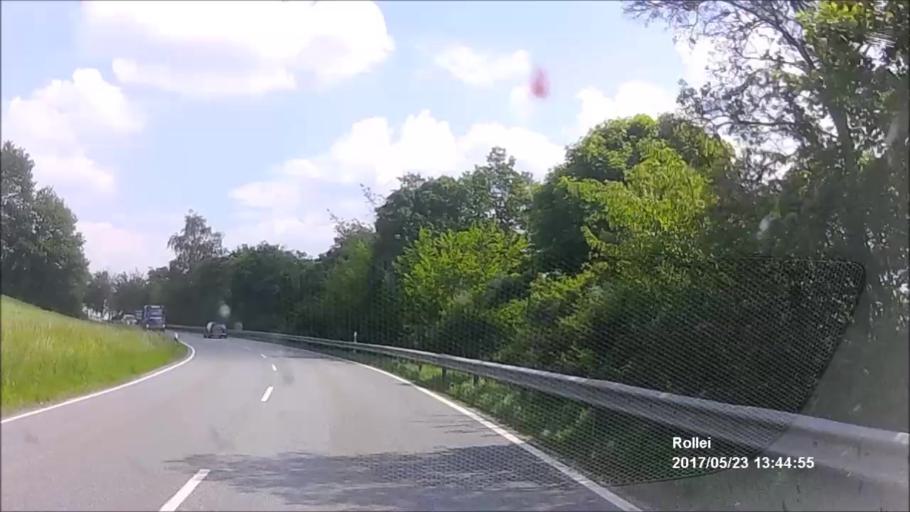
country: DE
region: Bavaria
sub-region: Upper Bavaria
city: Haag in Oberbayern
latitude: 48.1822
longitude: 12.1512
